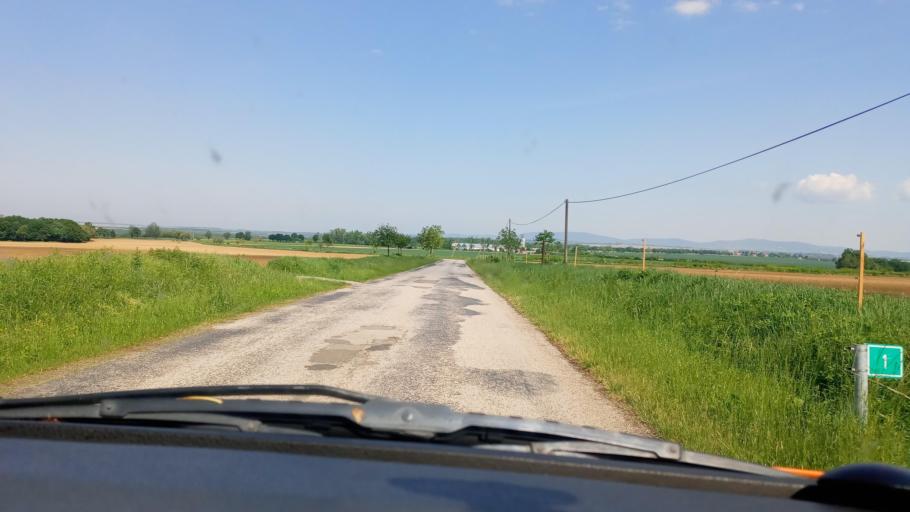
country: HU
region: Baranya
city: Harkany
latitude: 45.9123
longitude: 18.2428
